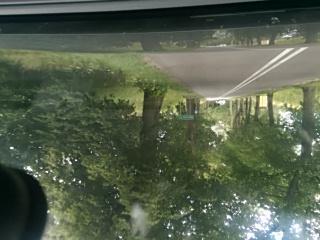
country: PL
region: Warmian-Masurian Voivodeship
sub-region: Powiat gizycki
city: Gizycko
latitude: 54.0203
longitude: 21.6627
